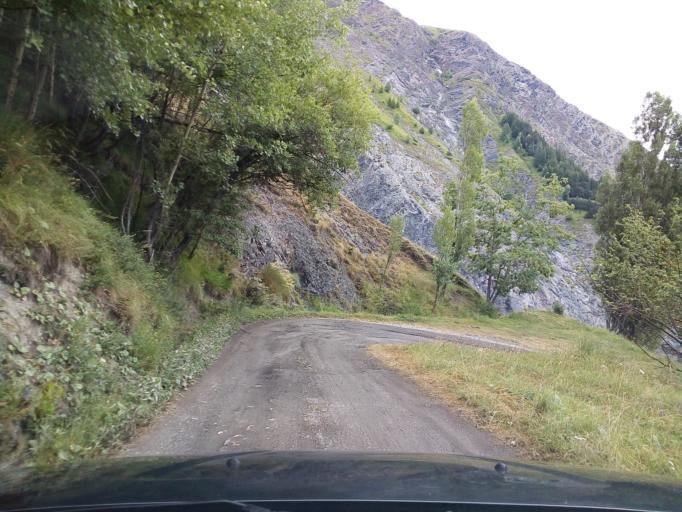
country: FR
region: Rhone-Alpes
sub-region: Departement de l'Isere
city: Mont-de-Lans
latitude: 45.0544
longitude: 6.1574
